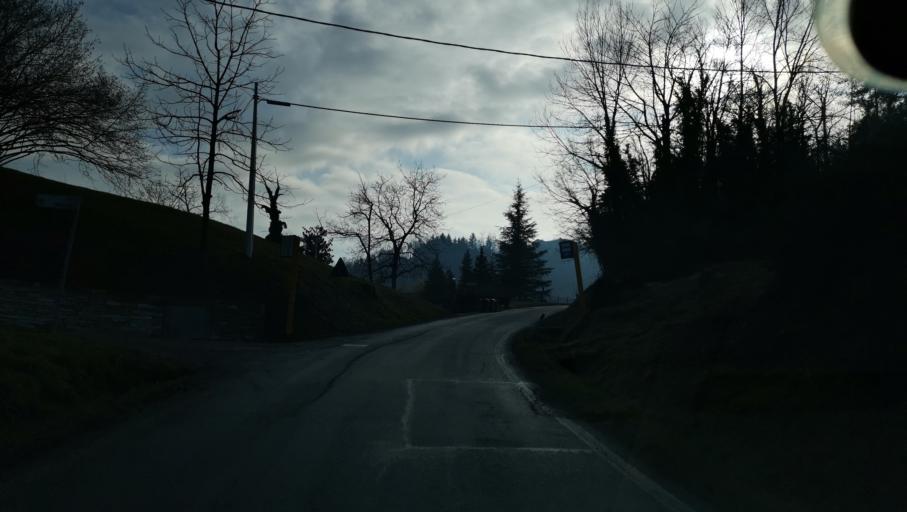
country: IT
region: Piedmont
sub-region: Provincia di Torino
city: Rivalba
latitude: 45.1029
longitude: 7.8912
